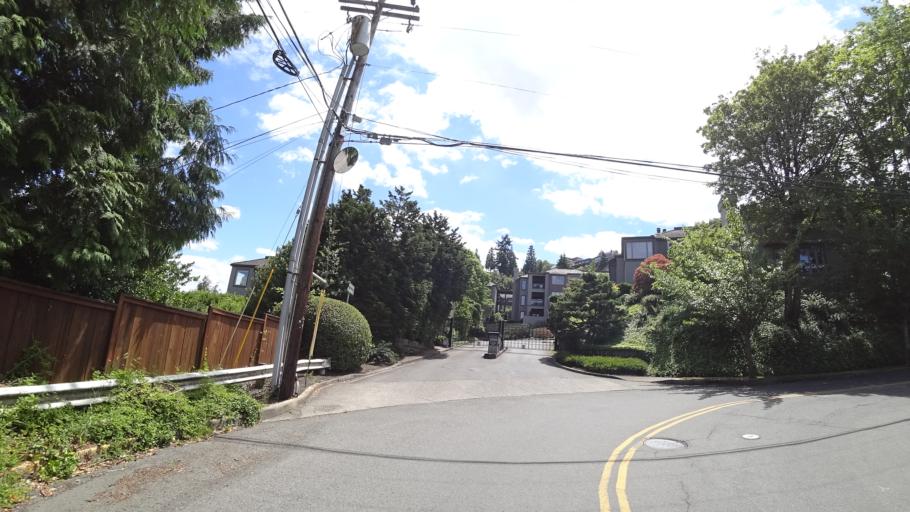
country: US
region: Oregon
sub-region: Multnomah County
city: Portland
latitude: 45.5283
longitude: -122.7037
